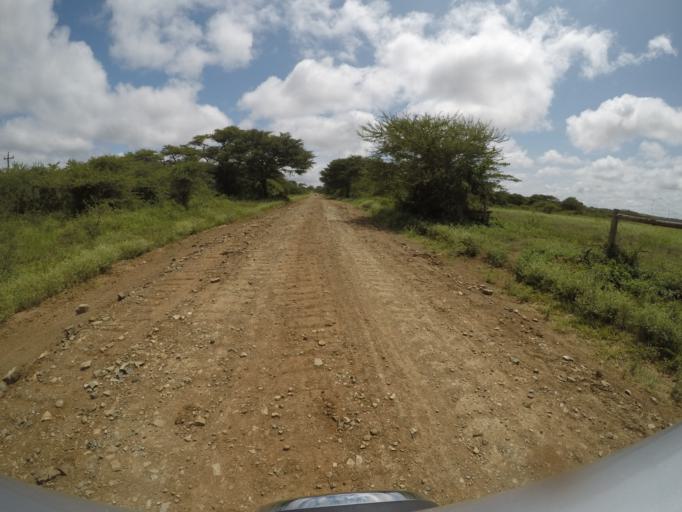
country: ZA
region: KwaZulu-Natal
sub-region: uThungulu District Municipality
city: Empangeni
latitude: -28.5703
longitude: 31.8368
